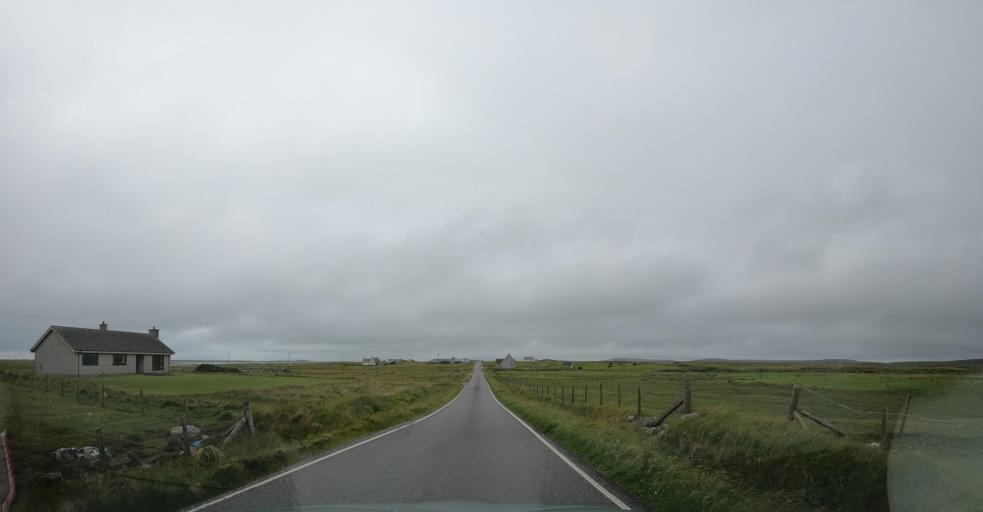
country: GB
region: Scotland
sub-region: Eilean Siar
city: Isle of North Uist
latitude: 57.5654
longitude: -7.3842
